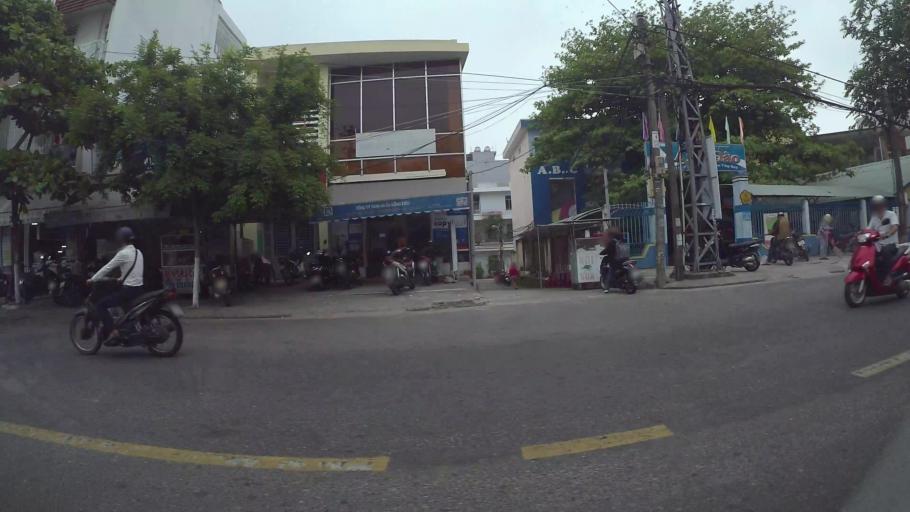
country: VN
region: Da Nang
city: Cam Le
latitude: 16.0325
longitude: 108.2228
